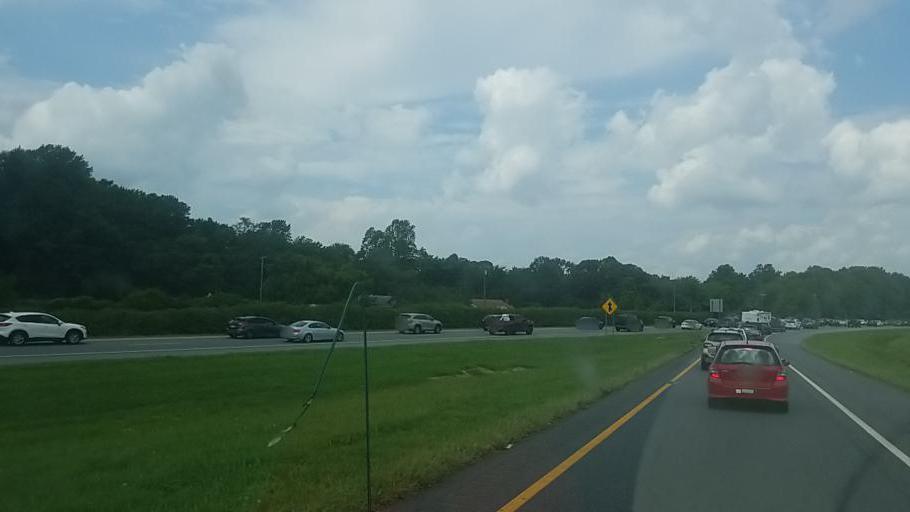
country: US
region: Delaware
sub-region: Sussex County
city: Milford
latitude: 38.9397
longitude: -75.4273
